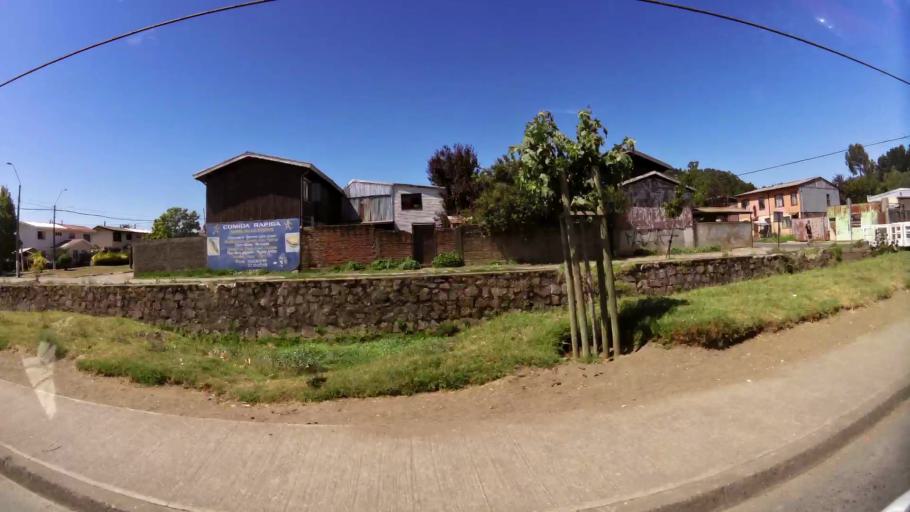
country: CL
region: Biobio
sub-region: Provincia de Concepcion
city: Penco
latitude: -36.7414
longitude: -72.9933
